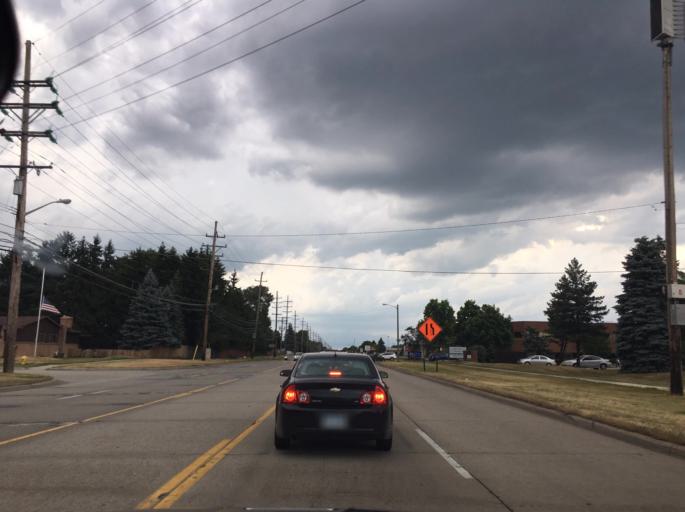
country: US
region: Michigan
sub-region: Macomb County
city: Clinton
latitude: 42.5930
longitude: -82.9522
